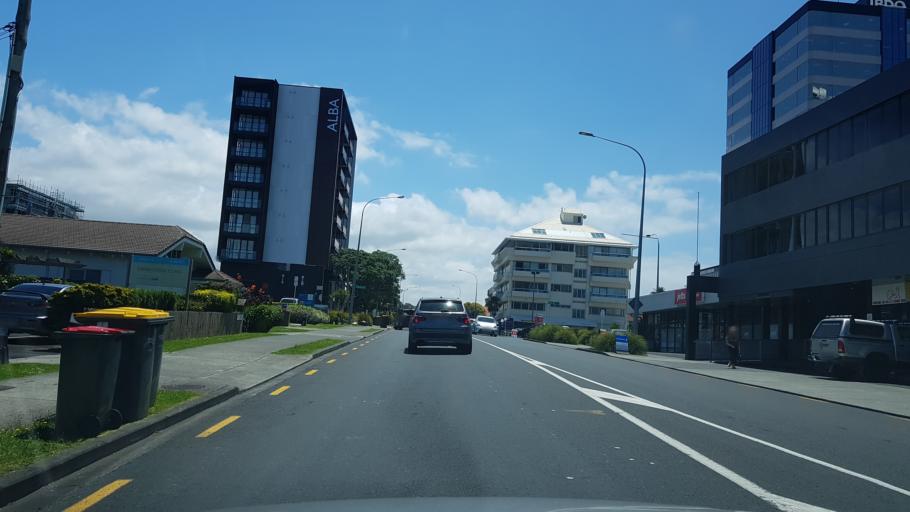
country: NZ
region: Auckland
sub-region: Auckland
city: North Shore
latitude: -36.7895
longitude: 174.7692
